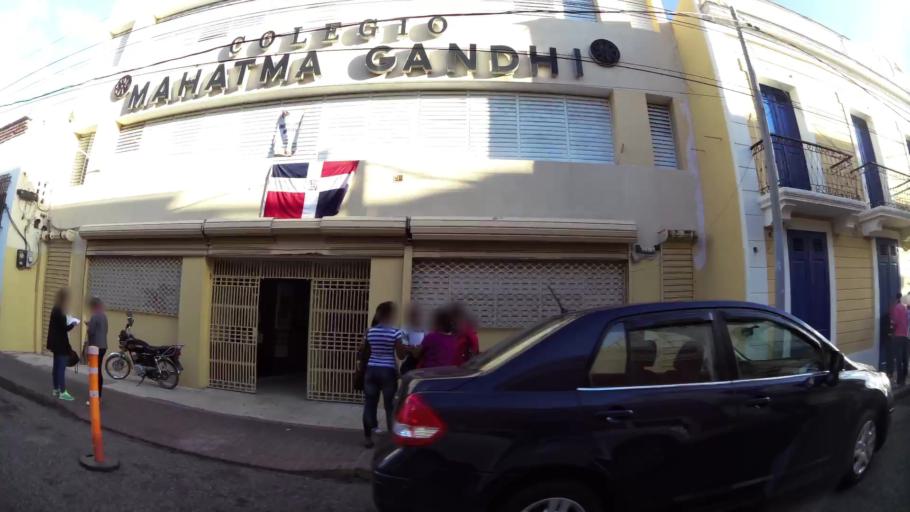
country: DO
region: Nacional
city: Ciudad Nueva
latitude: 18.4718
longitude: -69.8880
